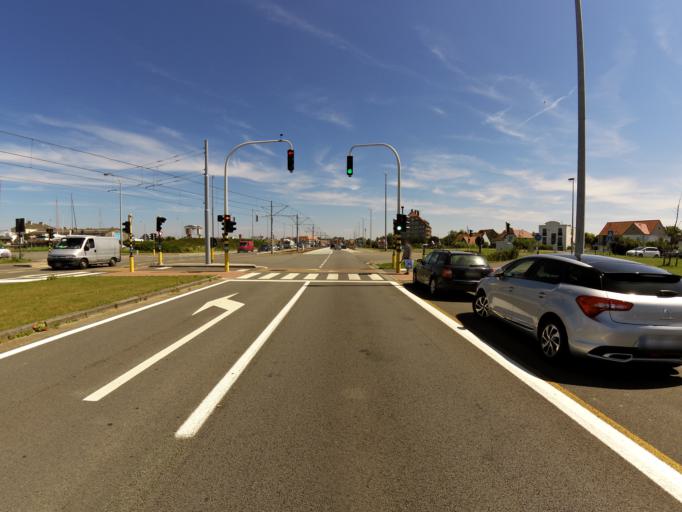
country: BE
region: Flanders
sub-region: Provincie West-Vlaanderen
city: Blankenberge
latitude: 51.3098
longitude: 3.1125
